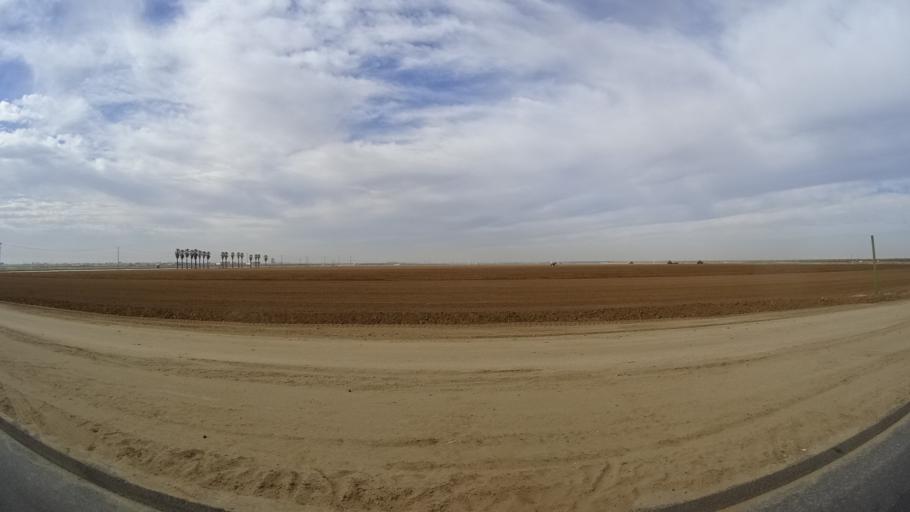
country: US
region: California
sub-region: Kern County
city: Rosedale
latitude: 35.4141
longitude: -119.1544
